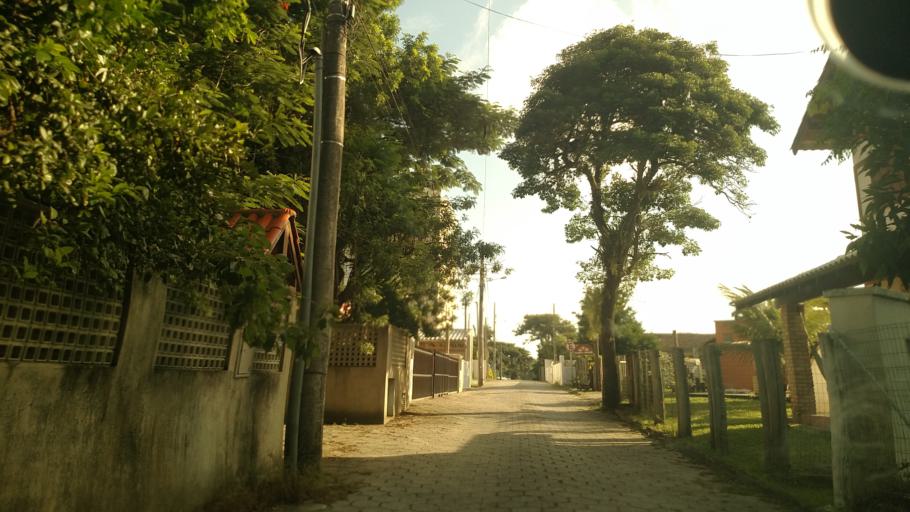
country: BR
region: Santa Catarina
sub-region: Porto Belo
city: Porto Belo
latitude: -27.1429
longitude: -48.5079
